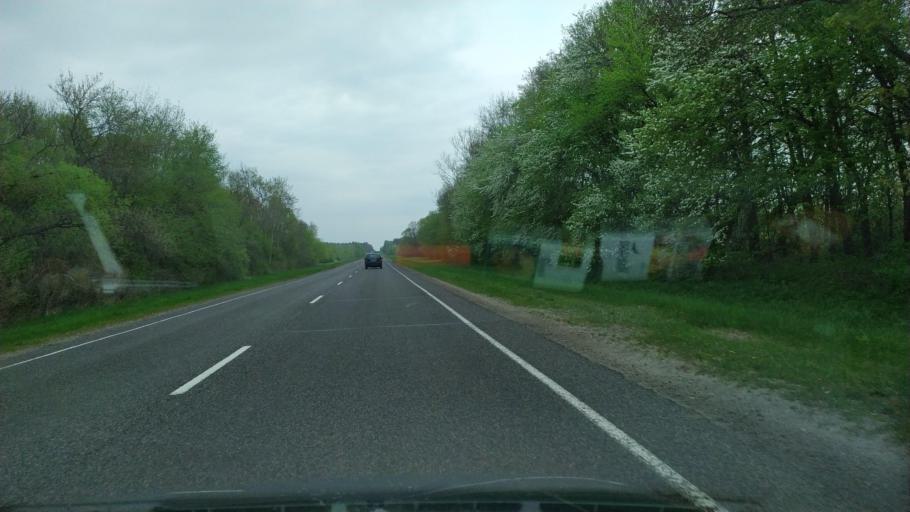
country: BY
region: Brest
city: Horad Kobryn
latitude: 52.2936
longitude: 24.5064
